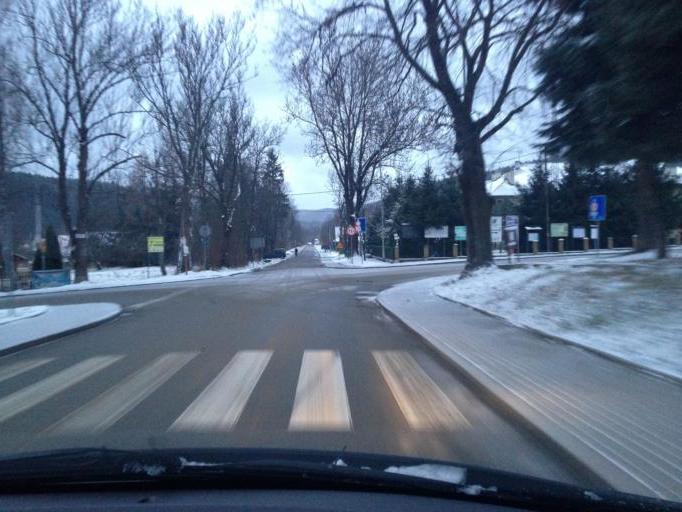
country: PL
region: Subcarpathian Voivodeship
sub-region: Powiat jasielski
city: Krempna
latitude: 49.5115
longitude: 21.5009
